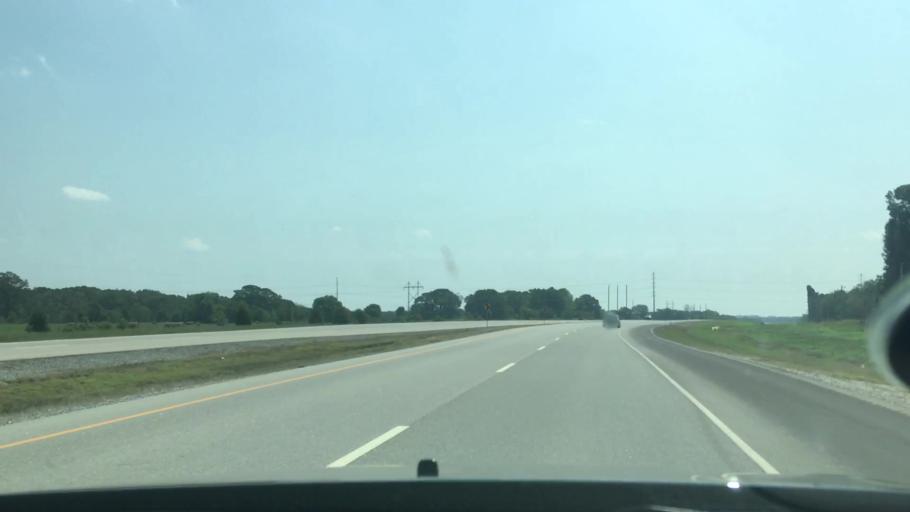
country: US
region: Oklahoma
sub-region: Atoka County
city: Atoka
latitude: 34.3358
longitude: -96.0573
